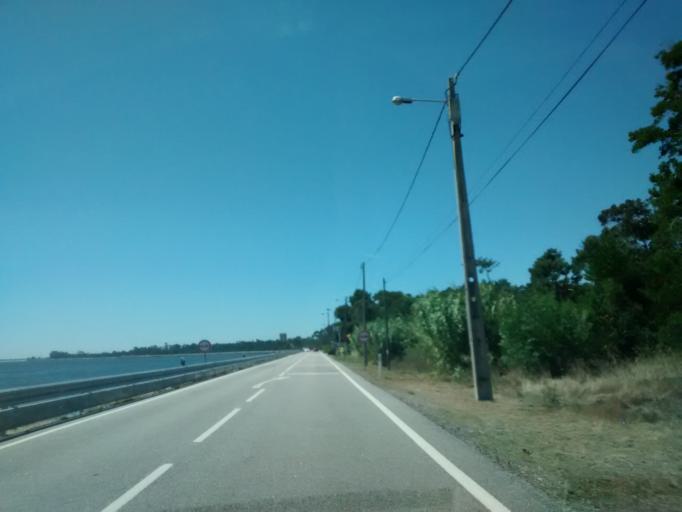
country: PT
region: Aveiro
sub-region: Ilhavo
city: Gafanha da Nazare
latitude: 40.7037
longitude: -8.7160
